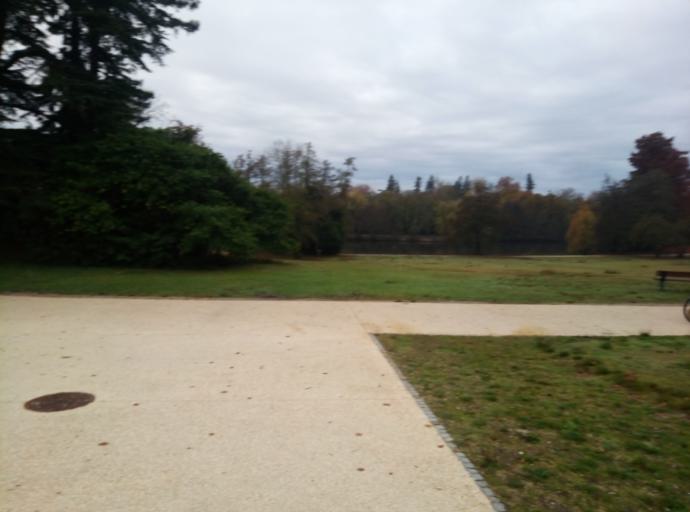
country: FR
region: Aquitaine
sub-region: Departement de la Gironde
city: Merignac
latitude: 44.8387
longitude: -0.6291
